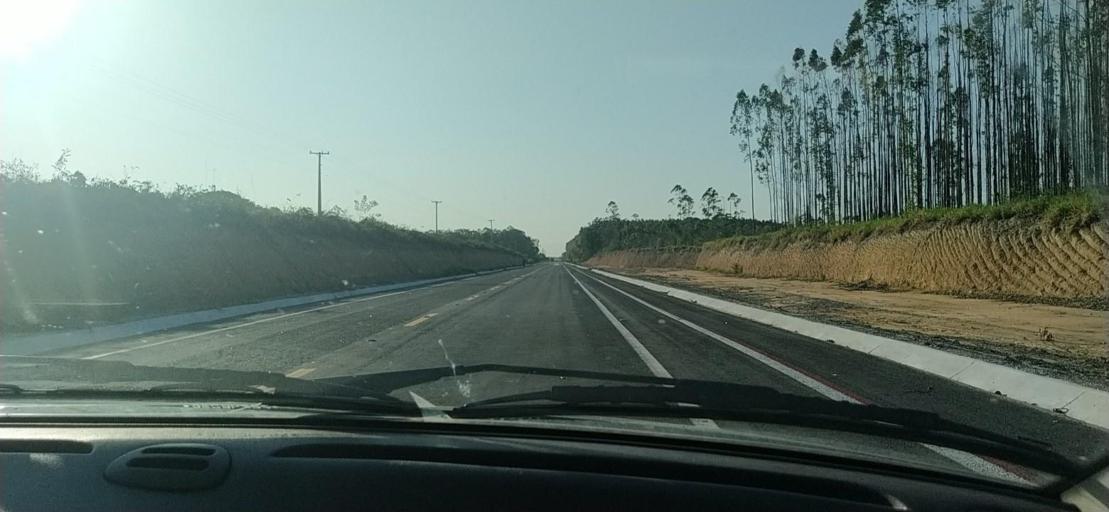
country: BR
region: Espirito Santo
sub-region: Conceicao Da Barra
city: Conceicao da Barra
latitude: -18.5592
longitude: -39.7729
